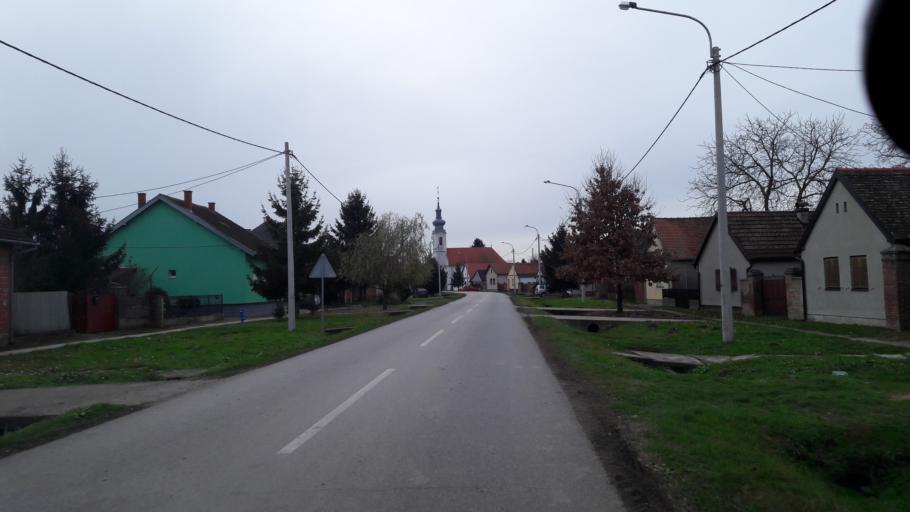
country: HR
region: Osjecko-Baranjska
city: Vladislavci
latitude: 45.4341
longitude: 18.5971
